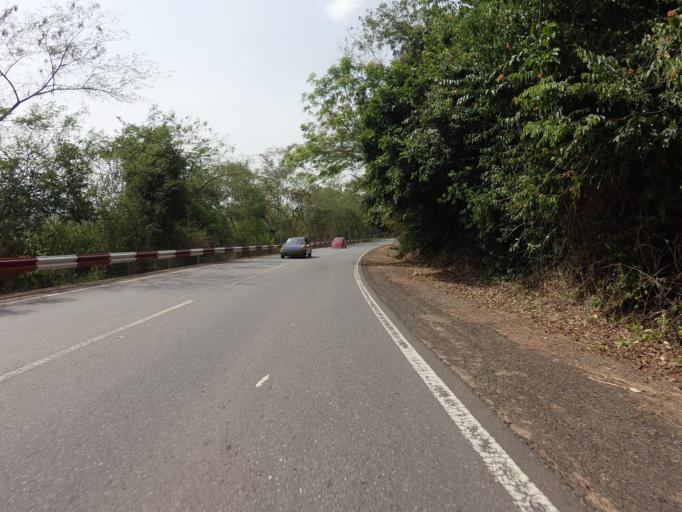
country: GH
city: Akropong
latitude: 6.2816
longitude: 0.0546
